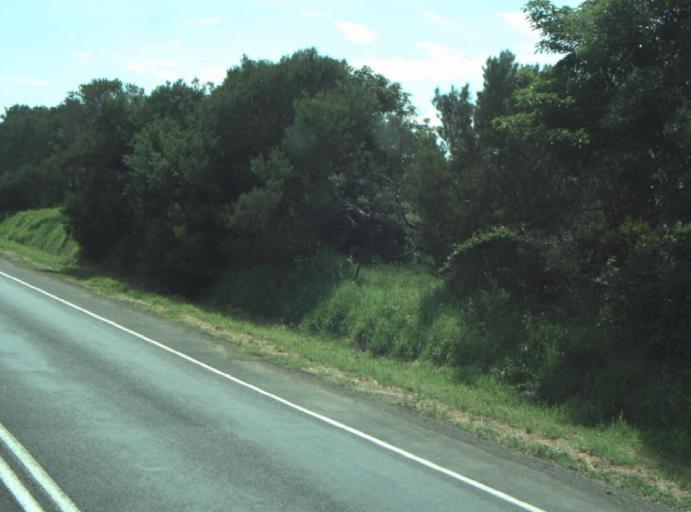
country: AU
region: Victoria
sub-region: Greater Geelong
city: Clifton Springs
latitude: -38.1582
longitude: 144.5855
